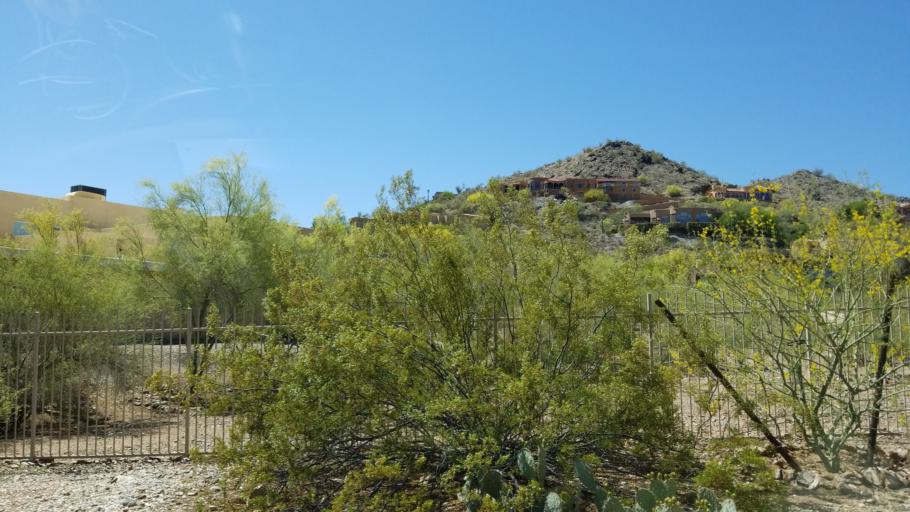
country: US
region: Arizona
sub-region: Maricopa County
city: Paradise Valley
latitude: 33.5609
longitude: -111.9793
